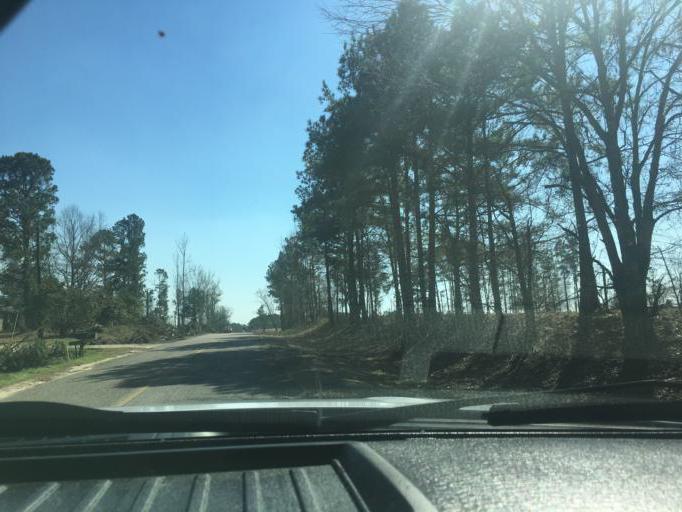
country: US
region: Alabama
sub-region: Lee County
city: Auburn
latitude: 32.4708
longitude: -85.4030
